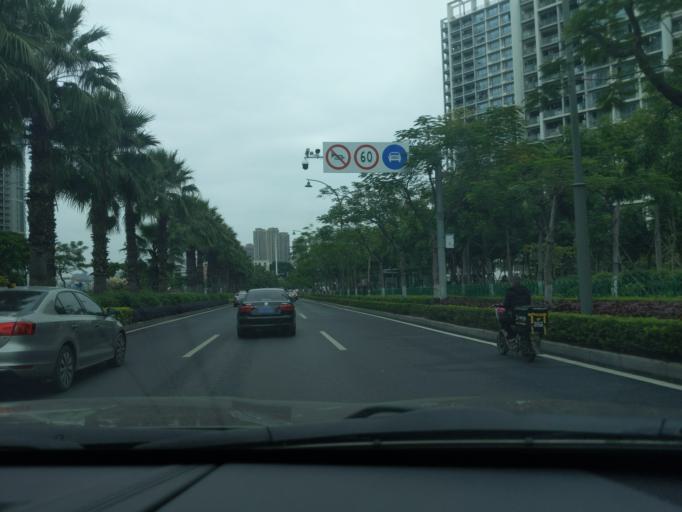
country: CN
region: Fujian
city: Liuwudian
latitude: 24.4941
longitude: 118.1704
